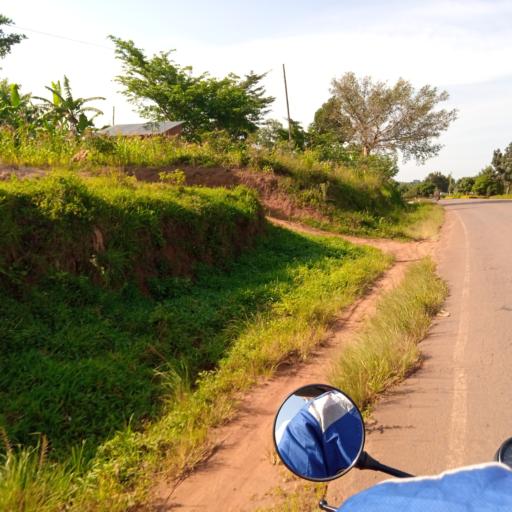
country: UG
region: Central Region
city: Masaka
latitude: -0.4361
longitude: 31.6623
